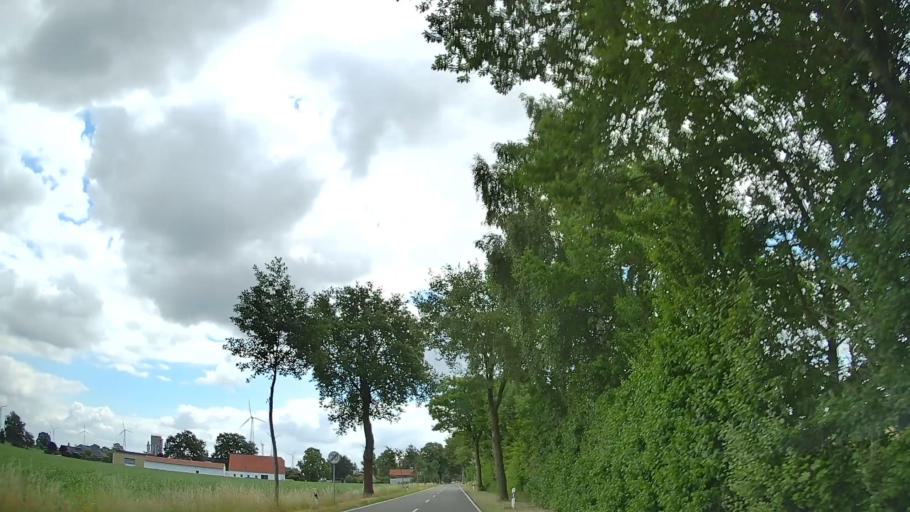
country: DE
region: Lower Saxony
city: Brockum
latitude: 52.4512
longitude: 8.4935
